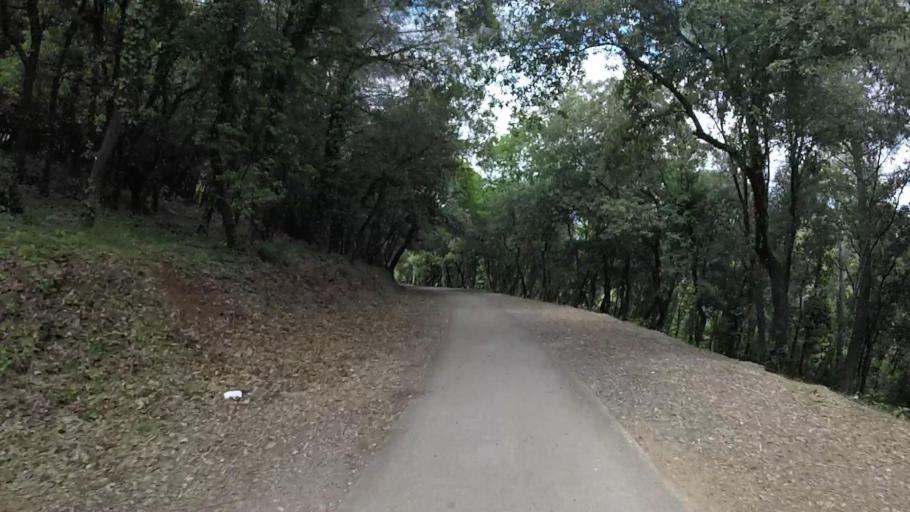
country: FR
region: Provence-Alpes-Cote d'Azur
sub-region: Departement des Alpes-Maritimes
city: Biot
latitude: 43.6165
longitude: 7.0892
